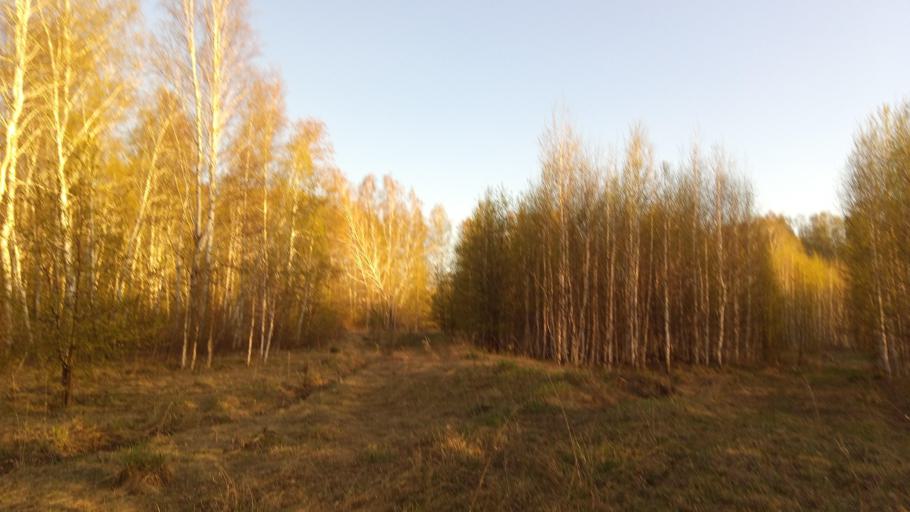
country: RU
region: Chelyabinsk
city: Timiryazevskiy
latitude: 54.9930
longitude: 60.8598
